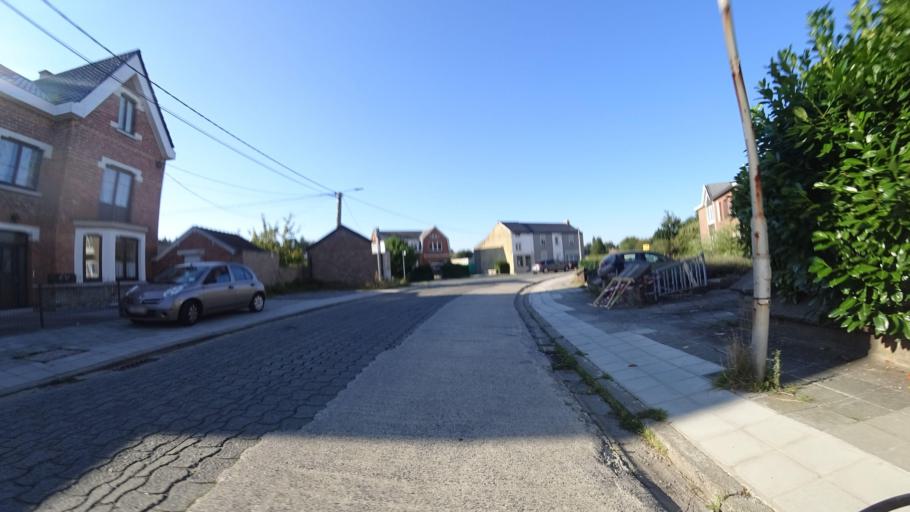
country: BE
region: Wallonia
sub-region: Province de Namur
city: Namur
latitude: 50.4733
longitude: 4.8292
